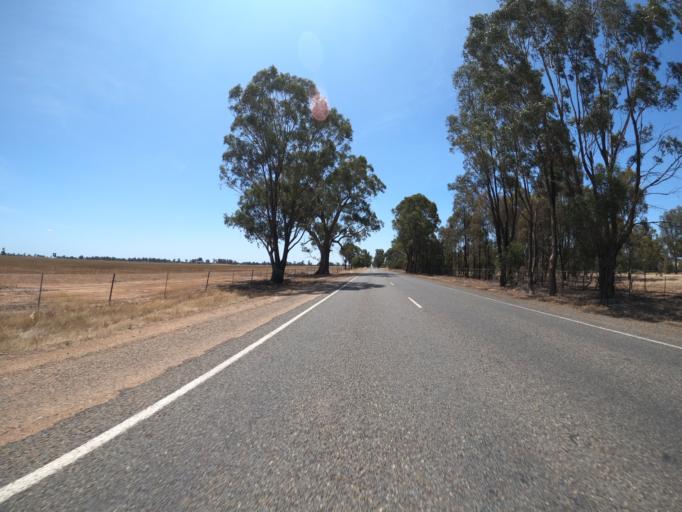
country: AU
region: Victoria
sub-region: Moira
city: Yarrawonga
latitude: -36.0677
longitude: 145.9955
